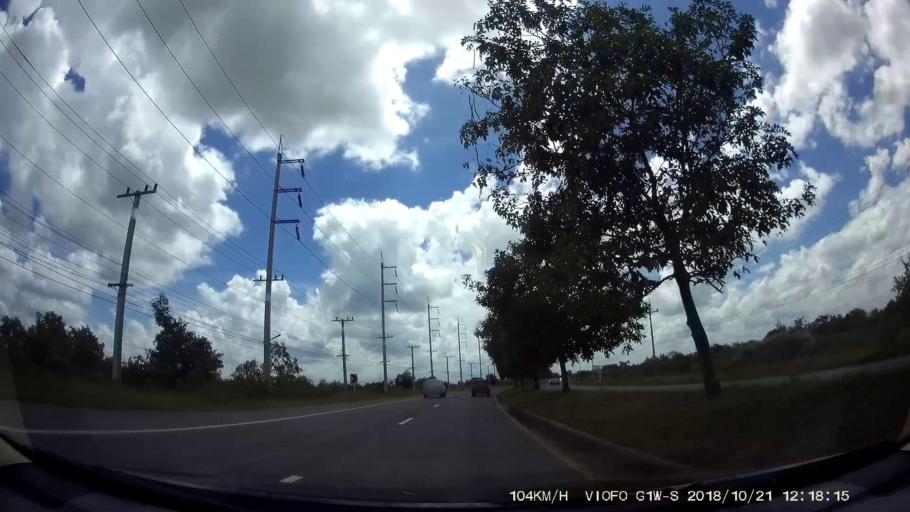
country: TH
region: Nakhon Ratchasima
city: Dan Khun Thot
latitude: 15.3192
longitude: 101.8181
